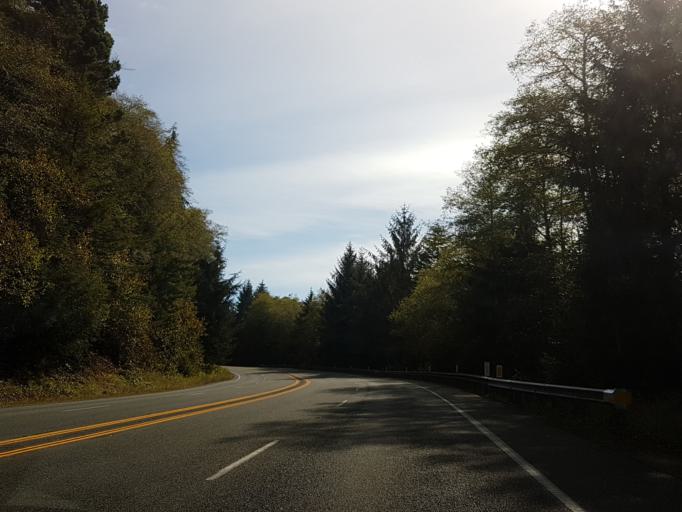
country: US
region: California
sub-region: Del Norte County
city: Bertsch-Oceanview
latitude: 41.4847
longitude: -124.0510
